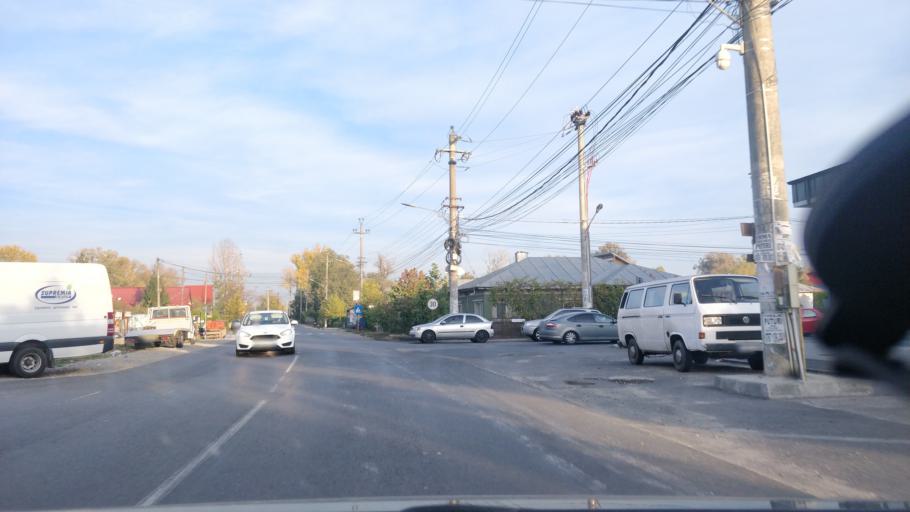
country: RO
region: Ilfov
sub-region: Comuna Ciorogarla
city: Ciorogarla
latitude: 44.4429
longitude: 25.8752
